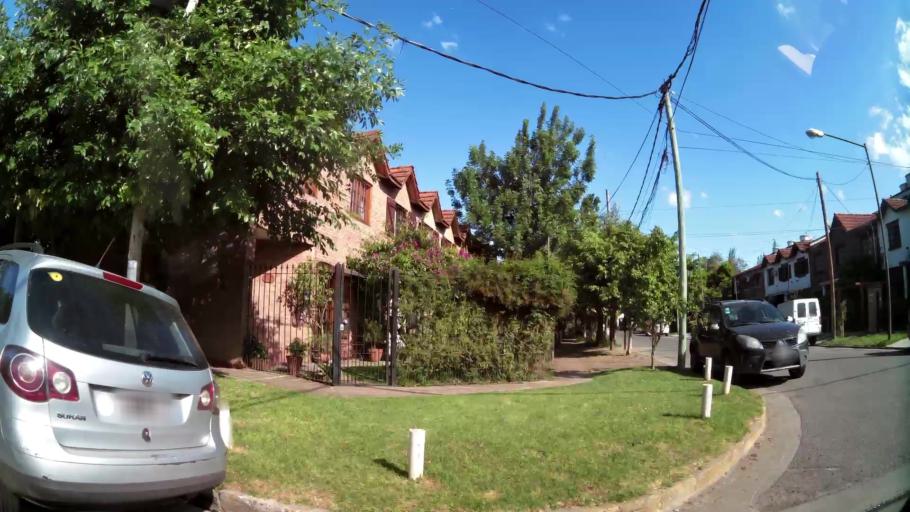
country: AR
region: Buenos Aires
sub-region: Partido de Tigre
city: Tigre
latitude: -34.4705
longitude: -58.5590
